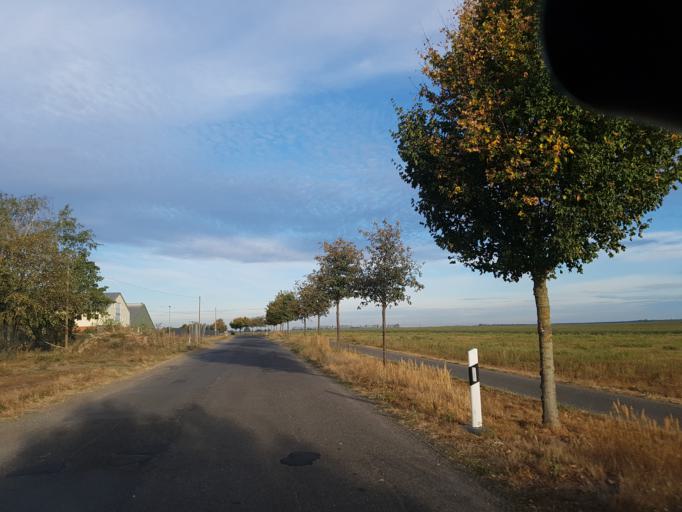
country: DE
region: Brandenburg
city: Dahme
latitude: 51.8586
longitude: 13.4091
